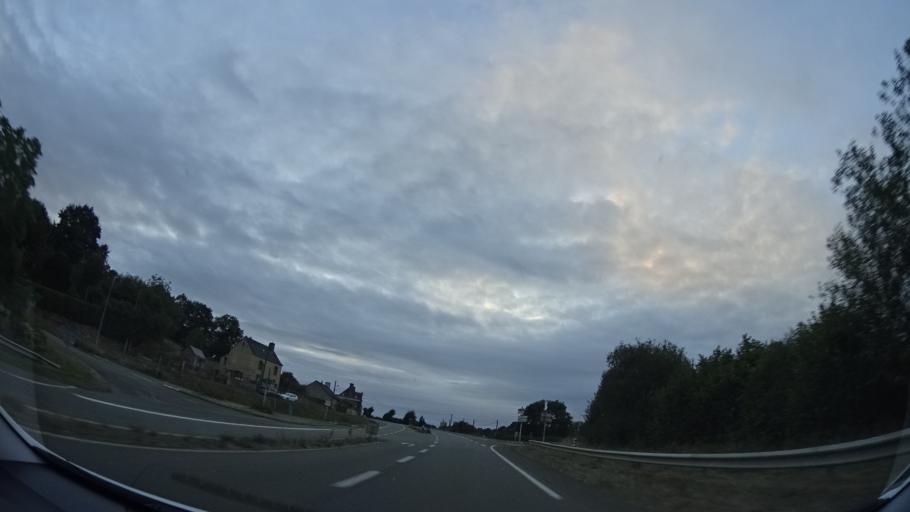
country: FR
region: Pays de la Loire
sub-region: Departement de la Mayenne
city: Sainte-Suzanne
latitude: 48.0375
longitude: -0.3897
